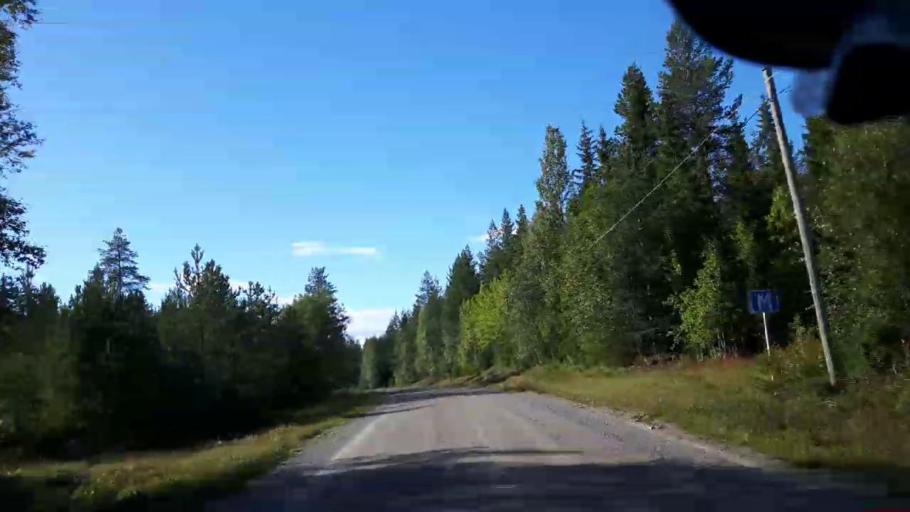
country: SE
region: Jaemtland
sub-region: Ragunda Kommun
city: Hammarstrand
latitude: 63.4841
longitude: 16.1117
